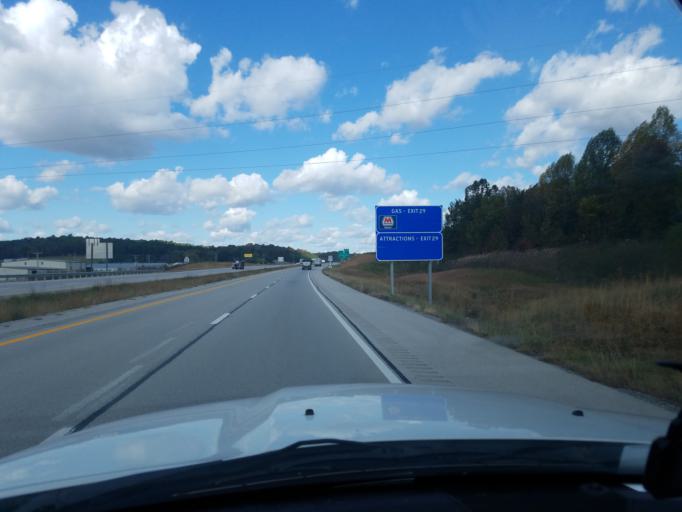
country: US
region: Kentucky
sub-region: Butler County
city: Morgantown
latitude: 37.2084
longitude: -86.7071
